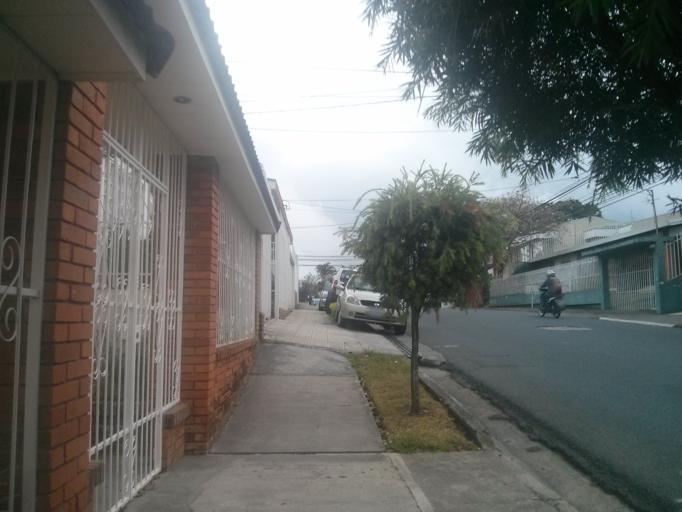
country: CR
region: San Jose
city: San Pedro
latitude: 9.9355
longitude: -84.0600
